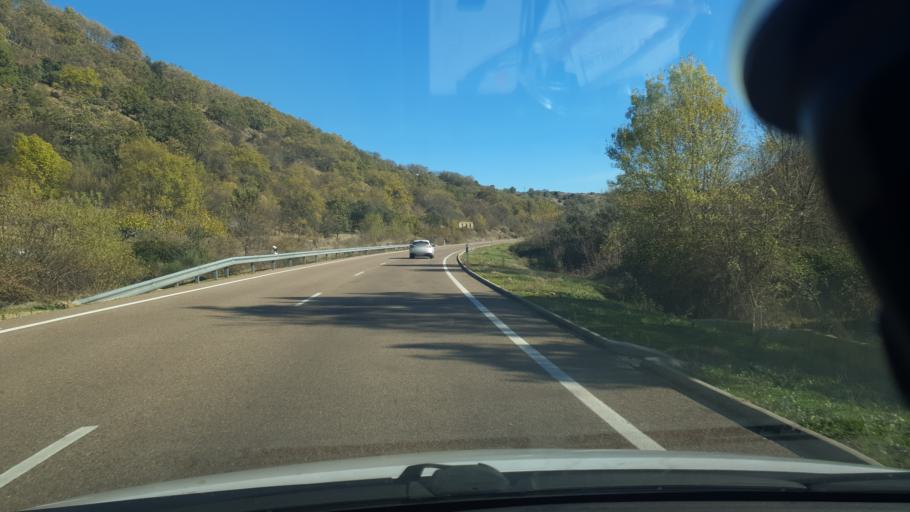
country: ES
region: Castille and Leon
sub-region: Provincia de Avila
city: Poyales del Hoyo
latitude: 40.1561
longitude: -5.1856
